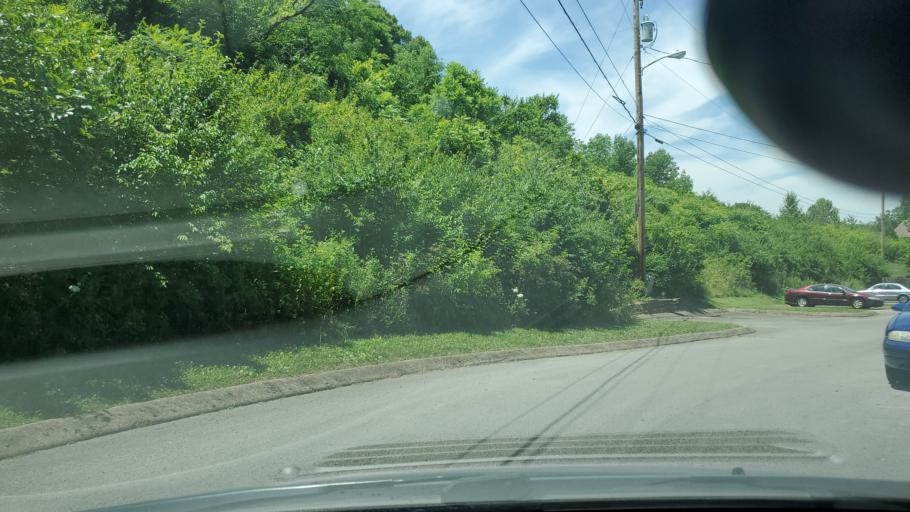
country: US
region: Tennessee
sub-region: Davidson County
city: Nashville
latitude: 36.2235
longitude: -86.7431
